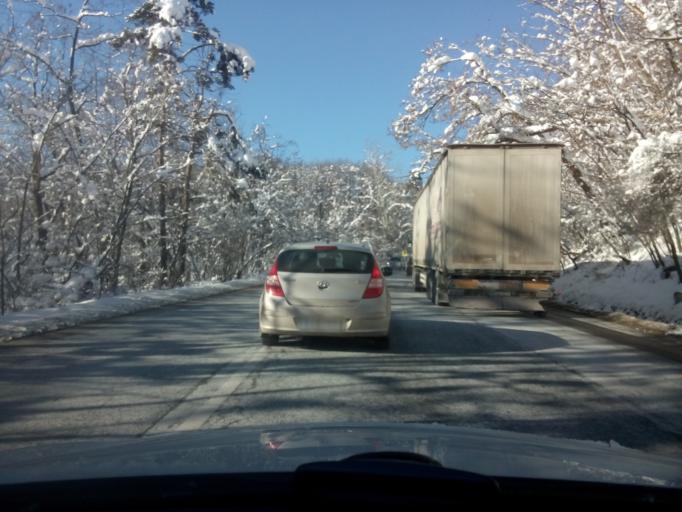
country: RO
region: Arges
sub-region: Comuna Cotmeana
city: Cotmeana
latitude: 44.9743
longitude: 24.6654
